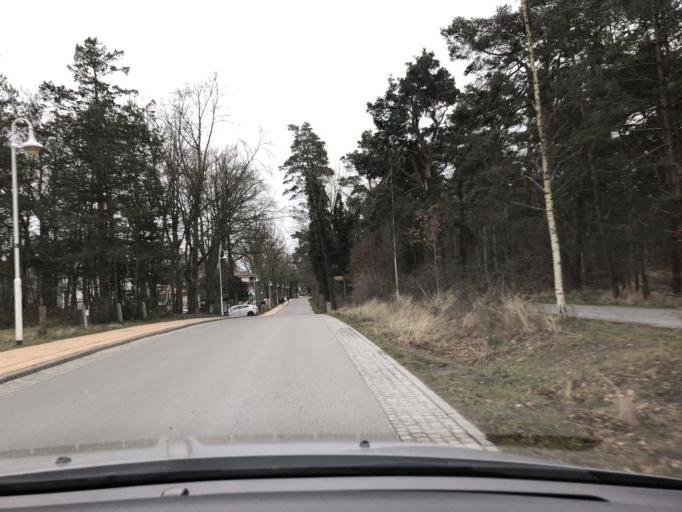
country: DE
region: Mecklenburg-Vorpommern
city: Ostseebad Prerow
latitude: 54.4509
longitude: 12.5558
